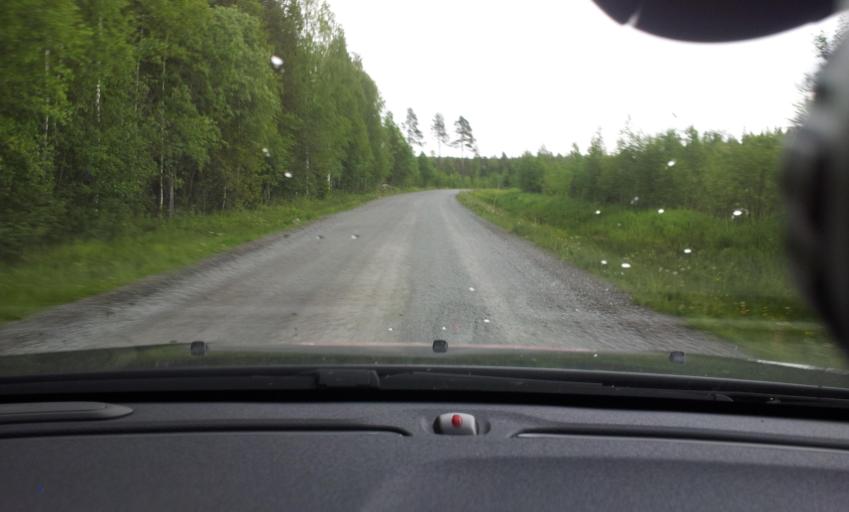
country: SE
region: Jaemtland
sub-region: OEstersunds Kommun
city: Brunflo
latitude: 63.1265
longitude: 15.0857
